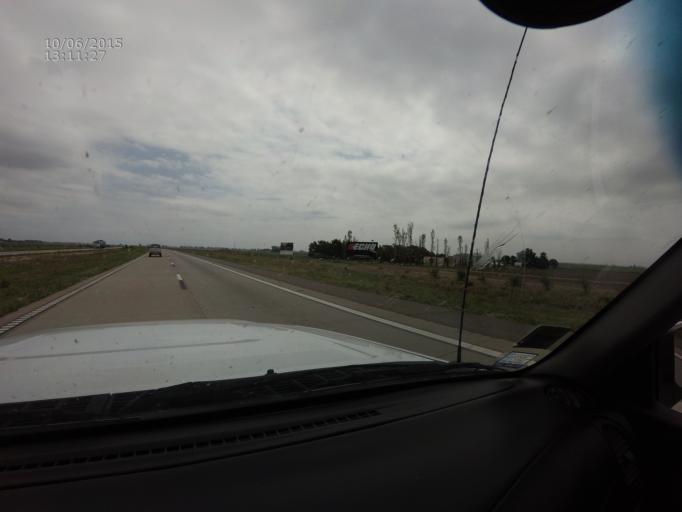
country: AR
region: Cordoba
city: General Roca
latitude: -32.7153
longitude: -61.8784
